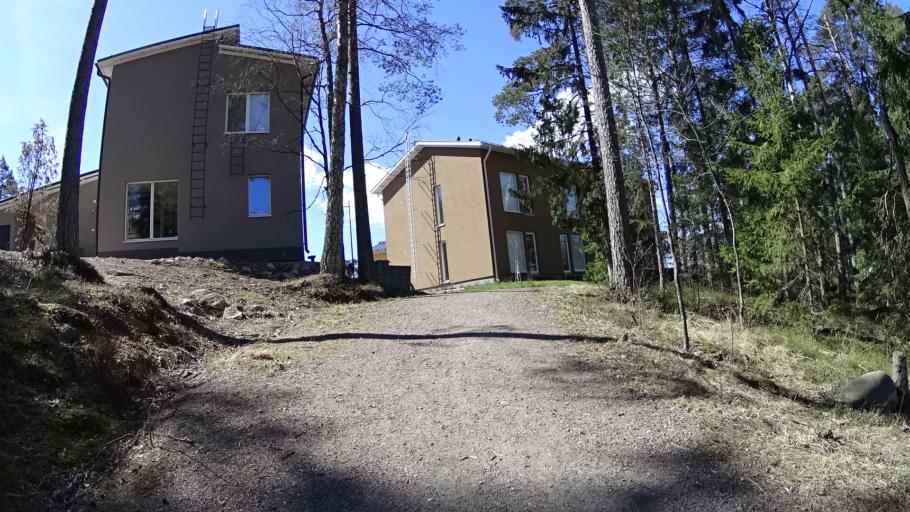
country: FI
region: Uusimaa
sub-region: Helsinki
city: Espoo
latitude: 60.1983
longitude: 24.6097
